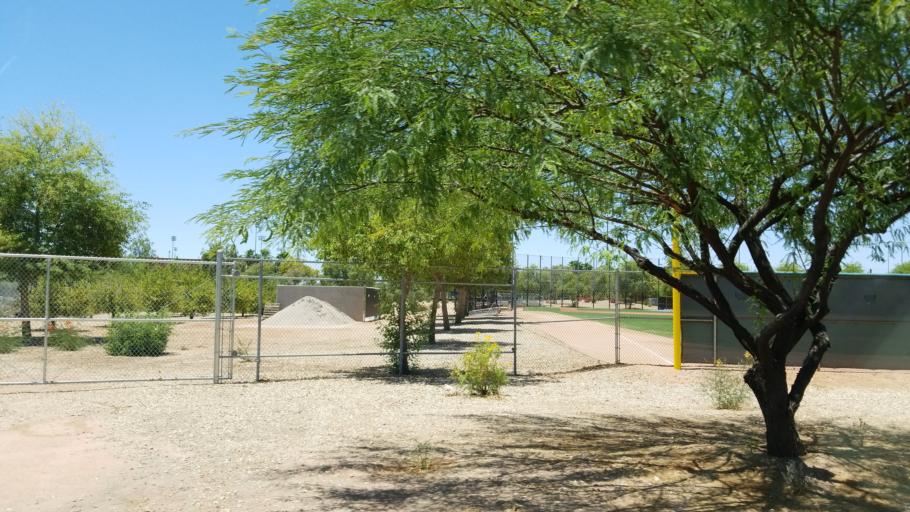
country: US
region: Arizona
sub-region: Maricopa County
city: Litchfield Park
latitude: 33.5128
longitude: -112.2909
